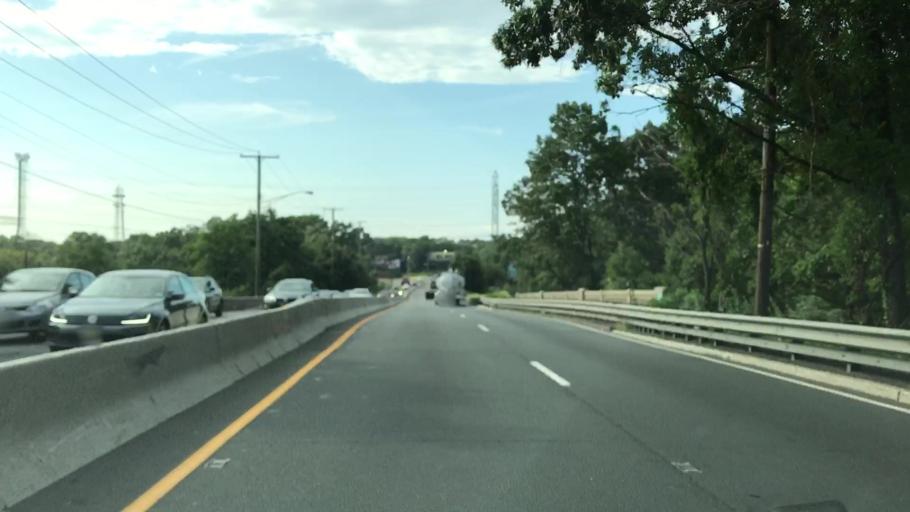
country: US
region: New Jersey
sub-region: Middlesex County
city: South Amboy
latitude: 40.4792
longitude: -74.2923
